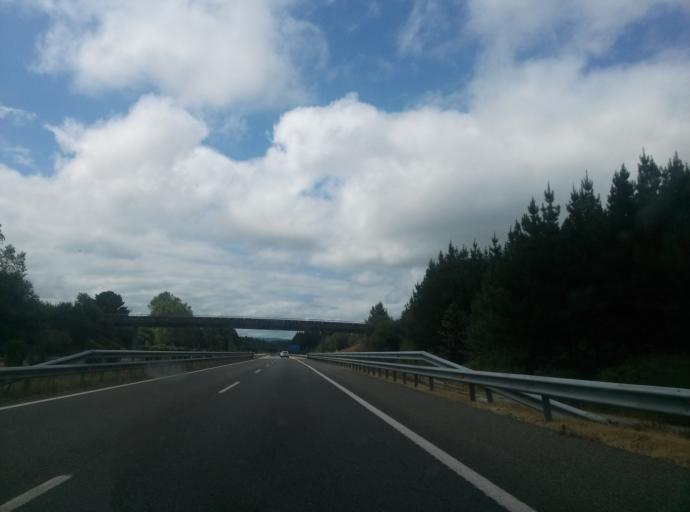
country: ES
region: Galicia
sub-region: Provincia de Lugo
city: Outeiro de Rei
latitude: 43.0938
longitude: -7.5901
